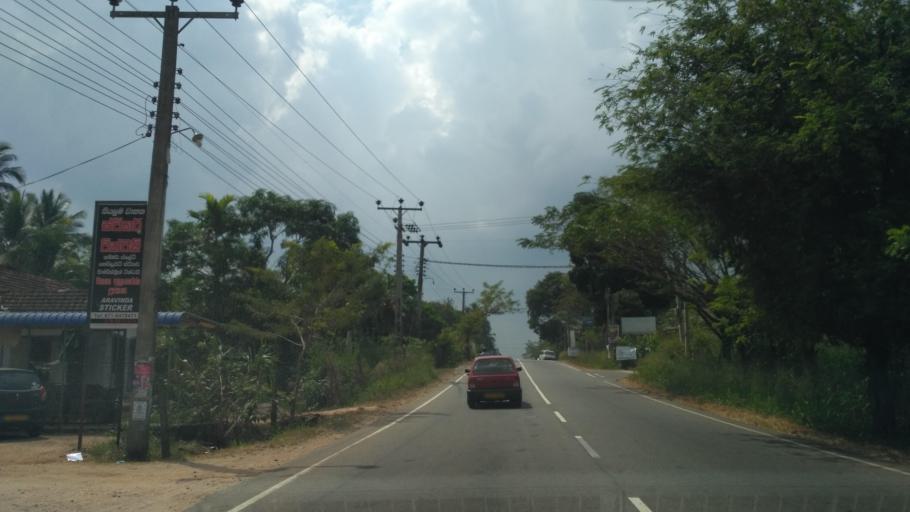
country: LK
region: North Western
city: Kuliyapitiya
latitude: 7.3262
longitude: 80.1138
